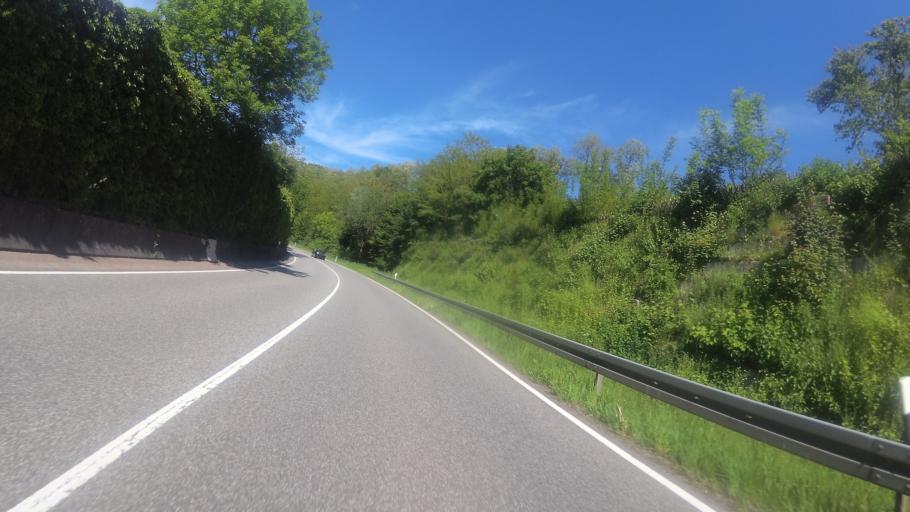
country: DE
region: Saarland
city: Quierschied
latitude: 49.3311
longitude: 7.0603
